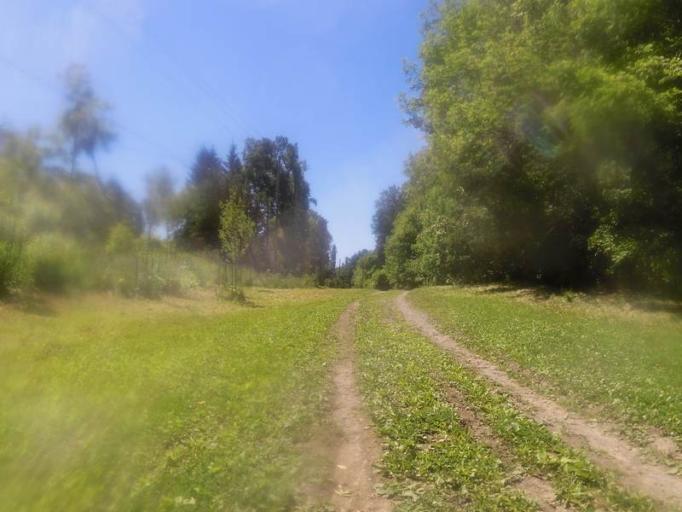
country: CA
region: Ontario
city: Kingston
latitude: 44.2476
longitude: -76.5351
